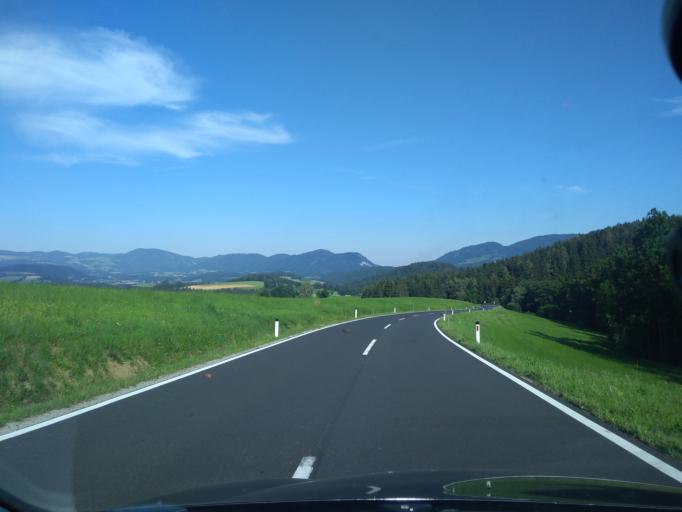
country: AT
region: Styria
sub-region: Politischer Bezirk Graz-Umgebung
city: Semriach
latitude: 47.2686
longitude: 15.4306
